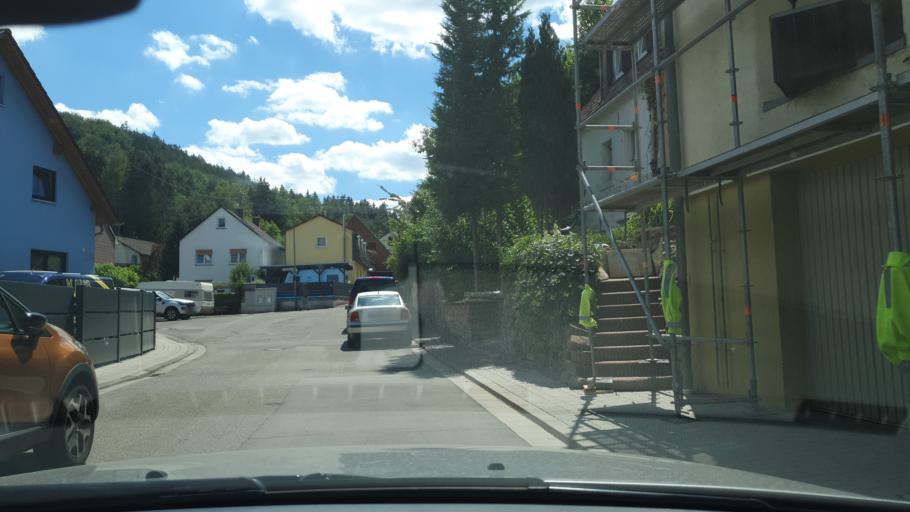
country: DE
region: Rheinland-Pfalz
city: Trippstadt
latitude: 49.3768
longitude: 7.8215
